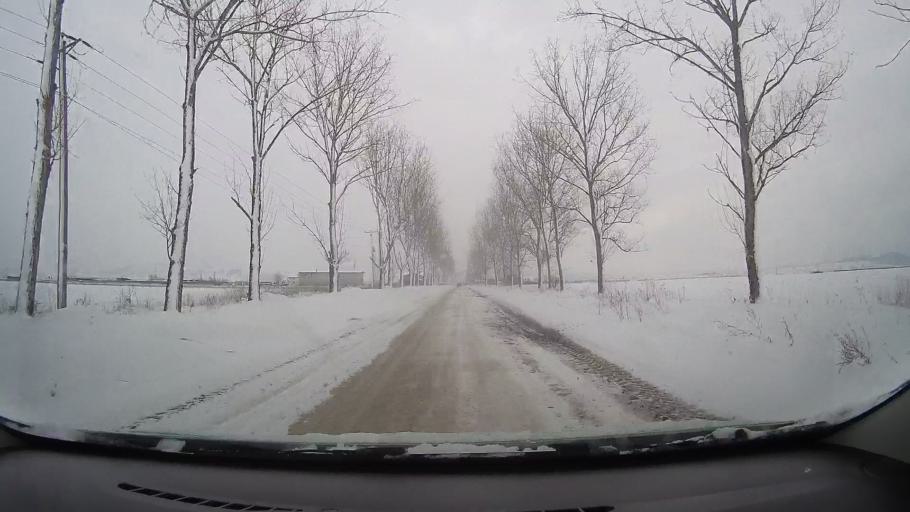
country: RO
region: Alba
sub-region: Municipiul Sebes
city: Lancram
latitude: 45.9603
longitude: 23.5253
